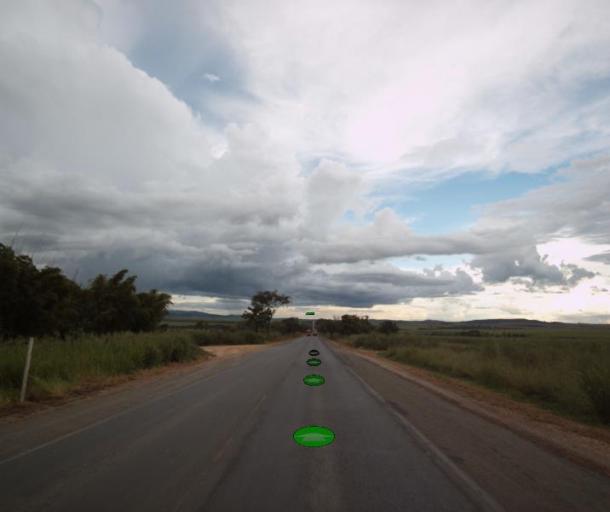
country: BR
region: Goias
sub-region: Itapaci
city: Itapaci
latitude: -14.8311
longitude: -49.3043
